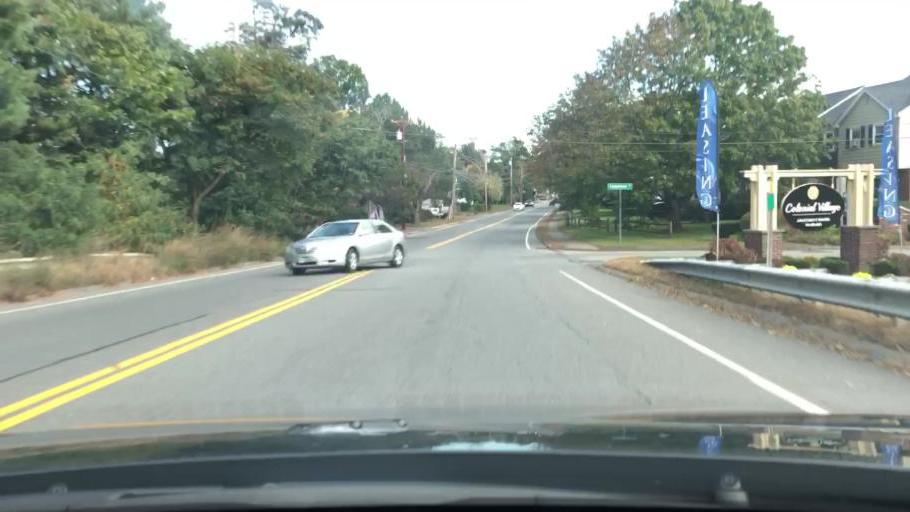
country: US
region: Massachusetts
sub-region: Essex County
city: Lawrence
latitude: 42.7455
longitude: -71.1373
